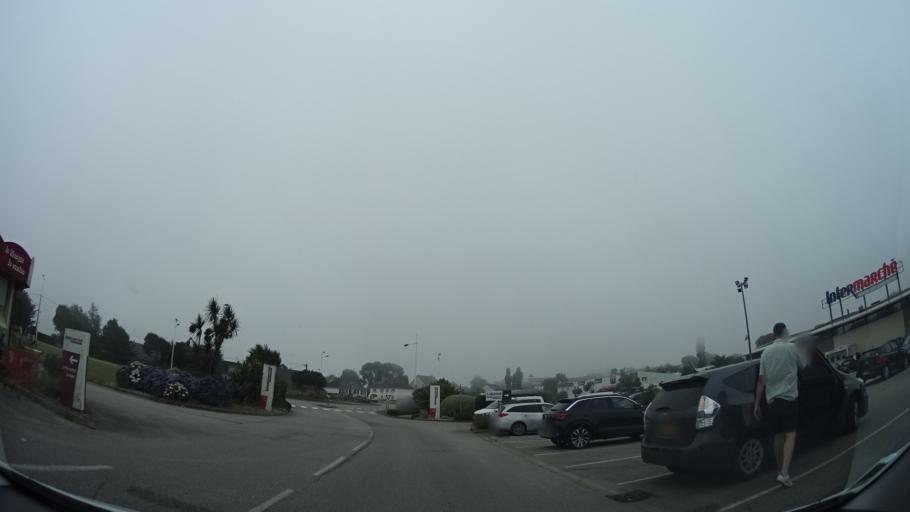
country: FR
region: Lower Normandy
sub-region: Departement de la Manche
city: Les Pieux
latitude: 49.5170
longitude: -1.7987
